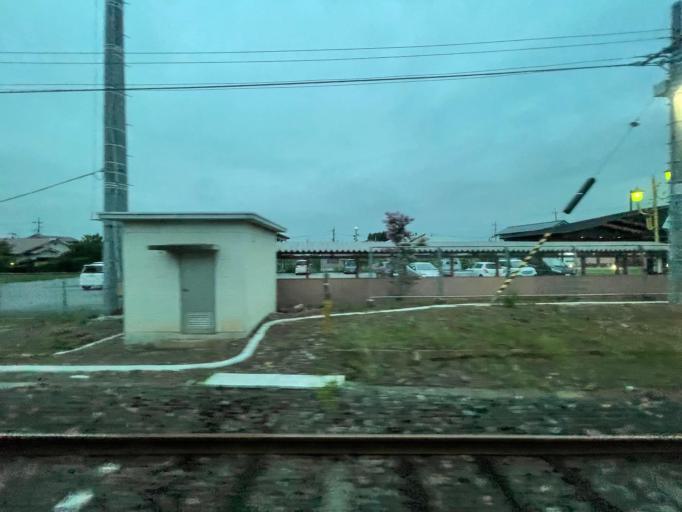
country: JP
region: Tochigi
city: Karasuyama
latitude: 36.6568
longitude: 140.0953
